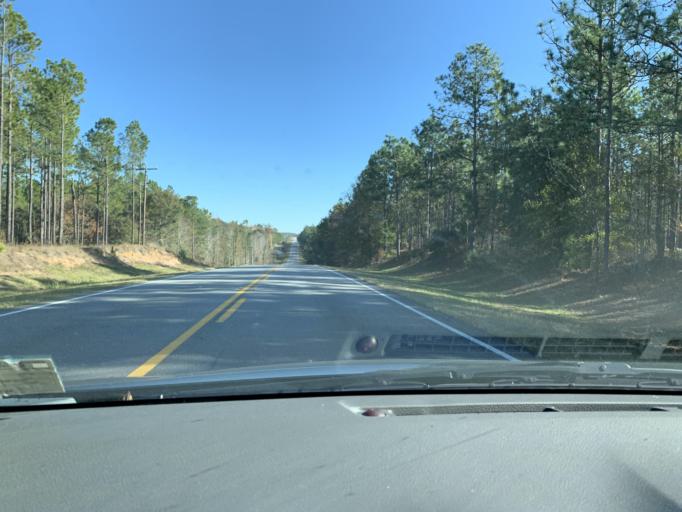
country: US
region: Georgia
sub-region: Ben Hill County
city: Fitzgerald
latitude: 31.7655
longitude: -83.1090
